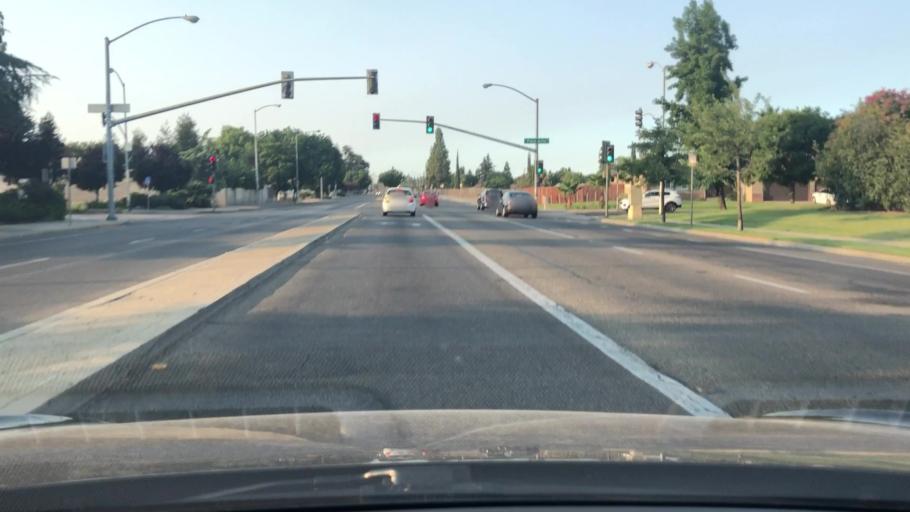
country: US
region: California
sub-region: Fresno County
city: Clovis
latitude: 36.8351
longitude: -119.7542
